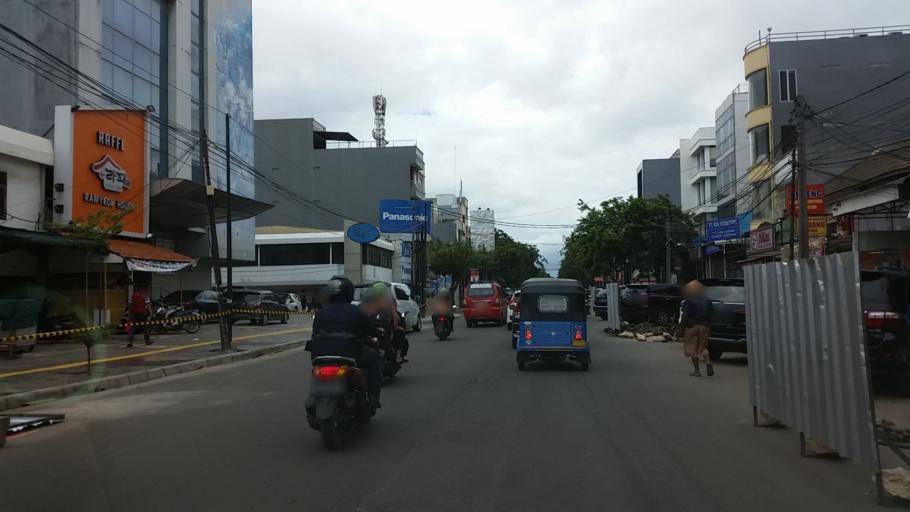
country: ID
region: Jakarta Raya
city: Jakarta
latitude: -6.1171
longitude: 106.7816
